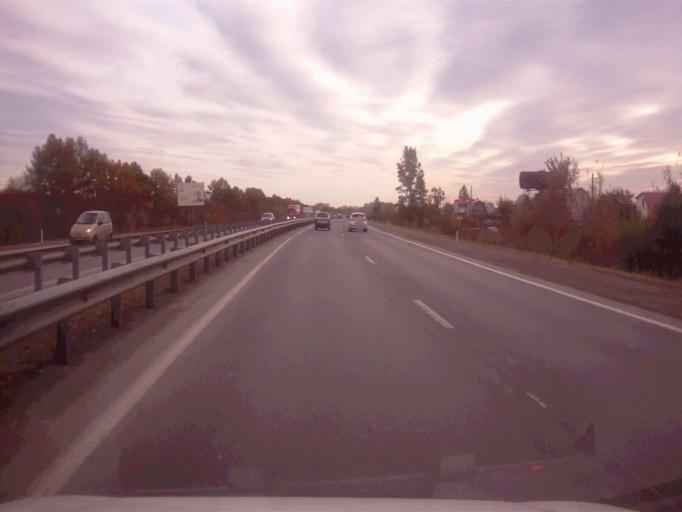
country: RU
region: Chelyabinsk
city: Novosineglazovskiy
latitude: 55.0269
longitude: 61.4498
